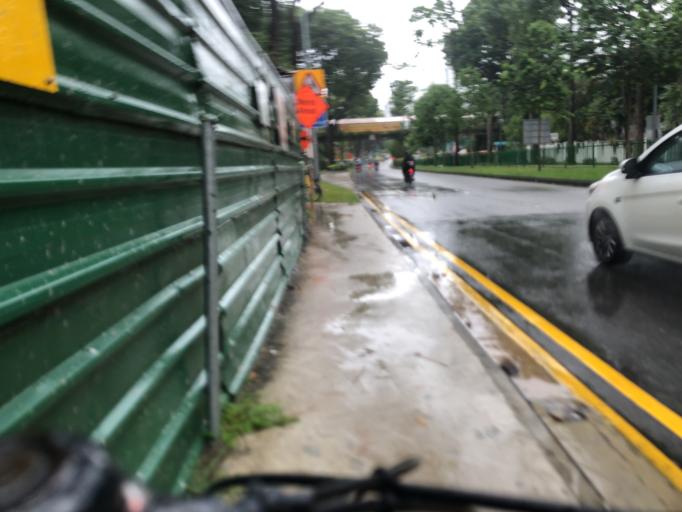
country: SG
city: Singapore
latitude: 1.3412
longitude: 103.7593
